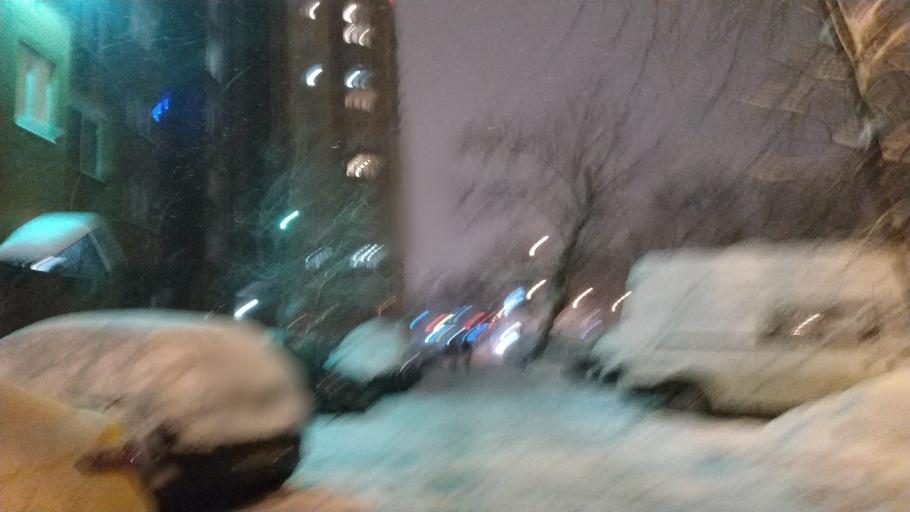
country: RU
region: Moscow
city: Zhulebino
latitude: 55.6925
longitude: 37.8626
